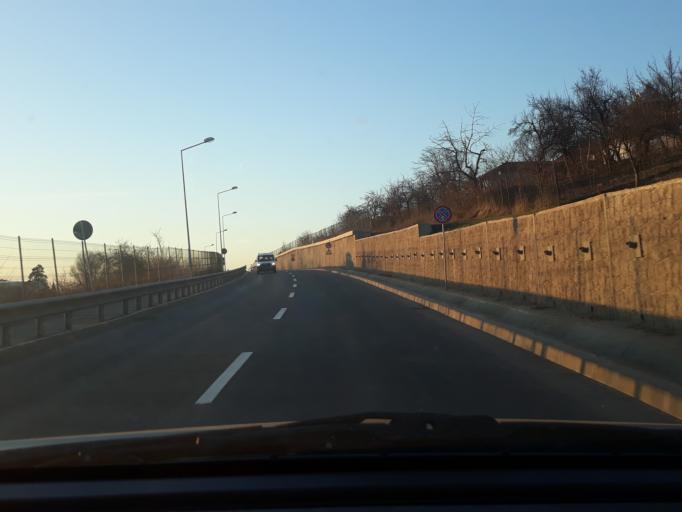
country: RO
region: Bihor
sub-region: Comuna Biharea
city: Oradea
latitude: 47.0598
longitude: 21.9463
